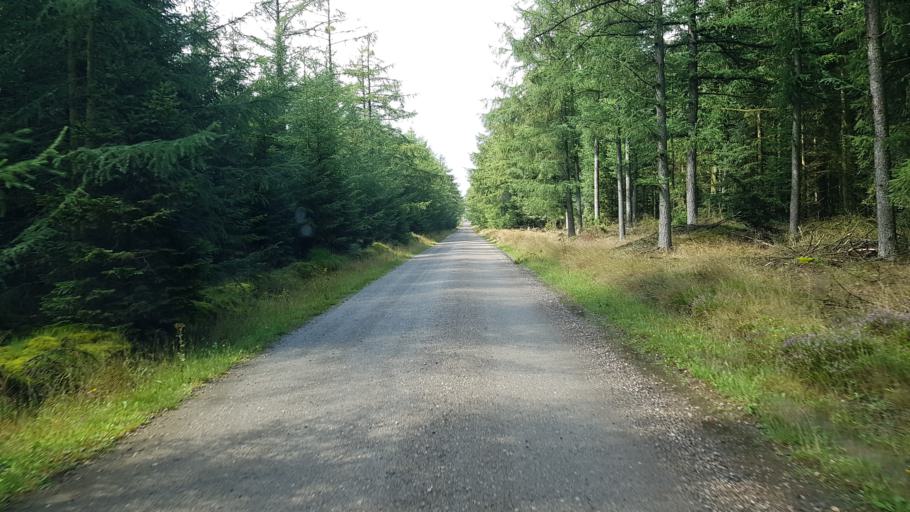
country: DK
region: South Denmark
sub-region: Vejen Kommune
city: Holsted
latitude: 55.5955
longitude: 8.8931
